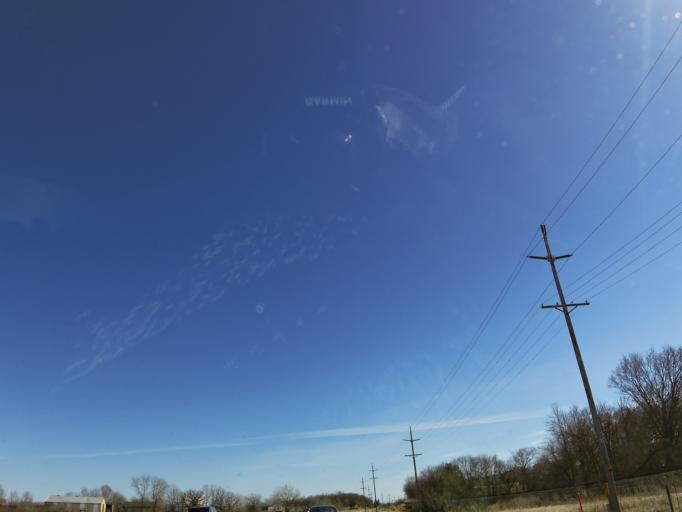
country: US
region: Minnesota
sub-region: Wright County
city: Buffalo
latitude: 45.1909
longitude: -93.8895
